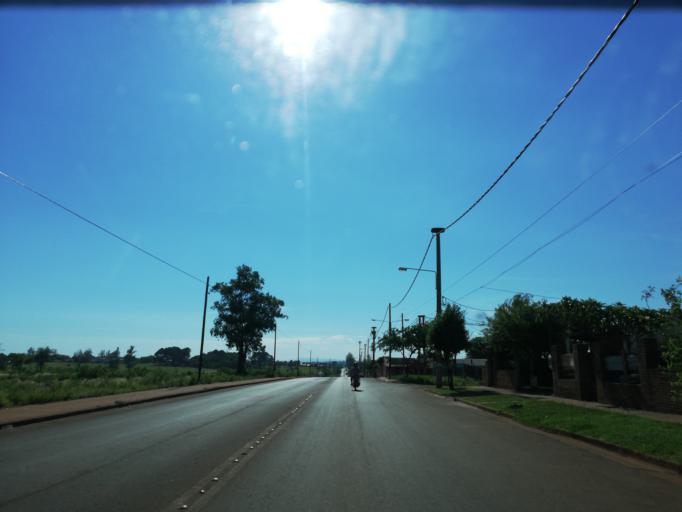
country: AR
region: Misiones
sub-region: Departamento de Capital
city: Posadas
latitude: -27.4331
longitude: -55.9397
